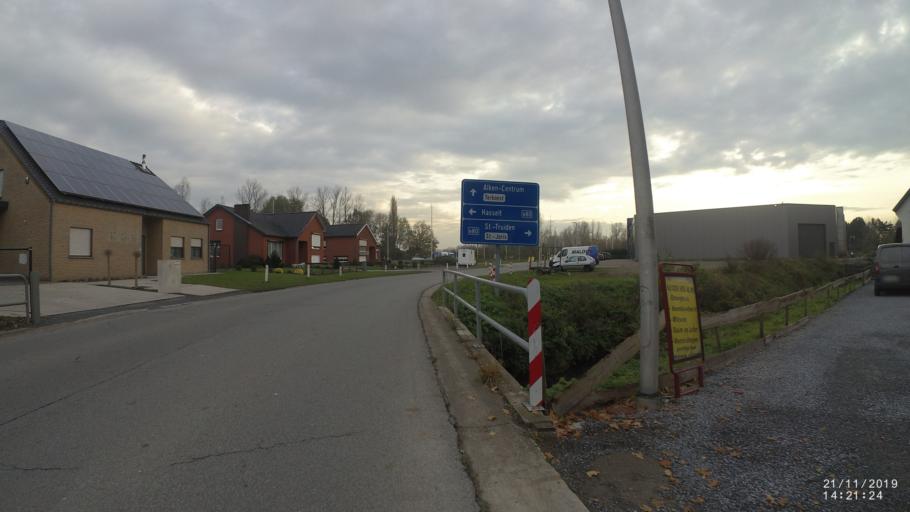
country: BE
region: Flanders
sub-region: Provincie Limburg
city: Alken
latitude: 50.8905
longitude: 5.3066
